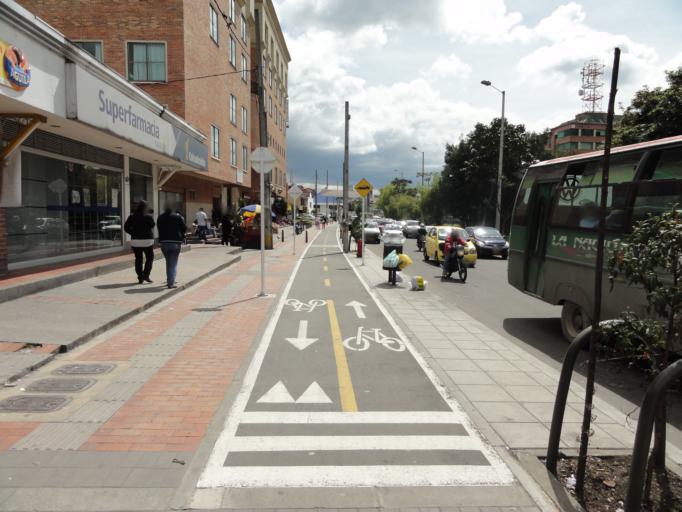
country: CO
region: Bogota D.C.
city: Barrio San Luis
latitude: 4.7041
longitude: -74.0442
